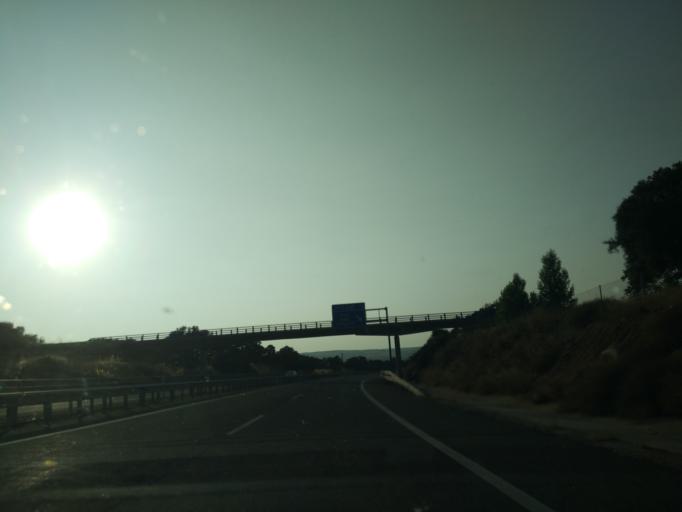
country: ES
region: Castille and Leon
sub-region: Provincia de Avila
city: Avila
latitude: 40.6712
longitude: -4.6750
